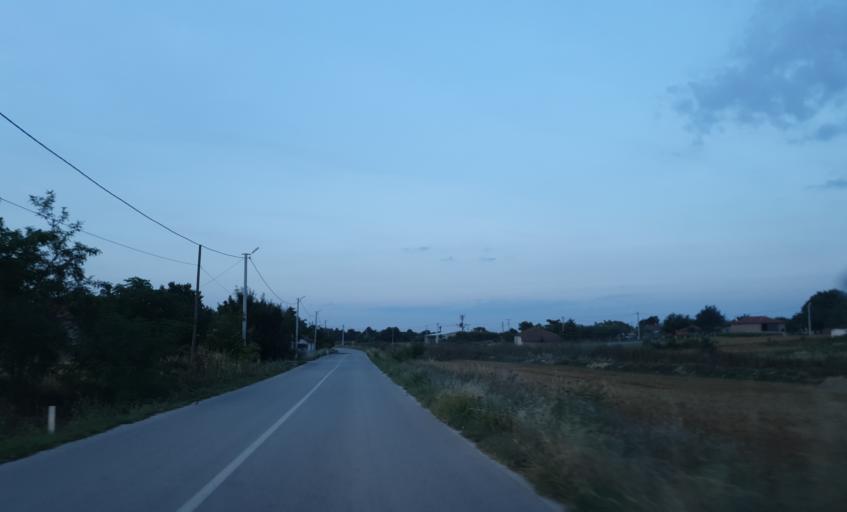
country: TR
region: Tekirdag
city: Beyazkoy
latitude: 41.4346
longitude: 27.6936
